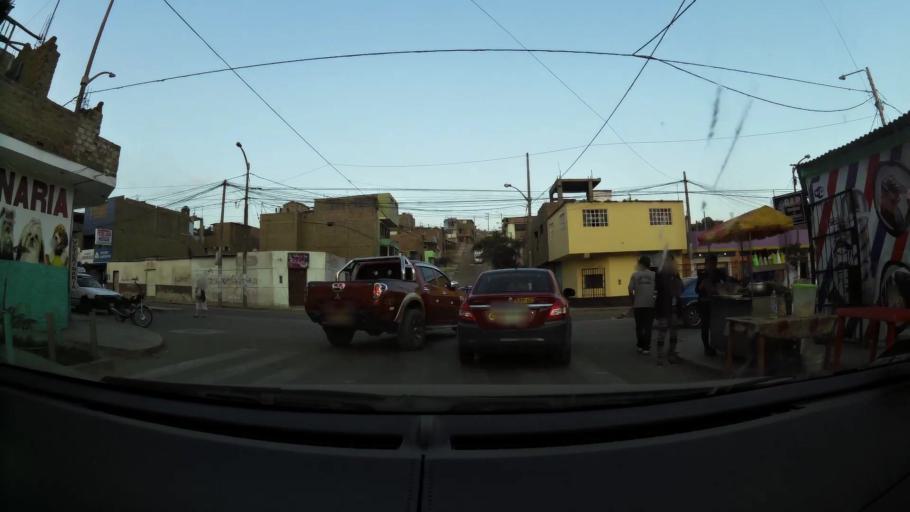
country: PE
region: La Libertad
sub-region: Provincia de Trujillo
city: El Porvenir
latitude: -8.0800
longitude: -79.0004
